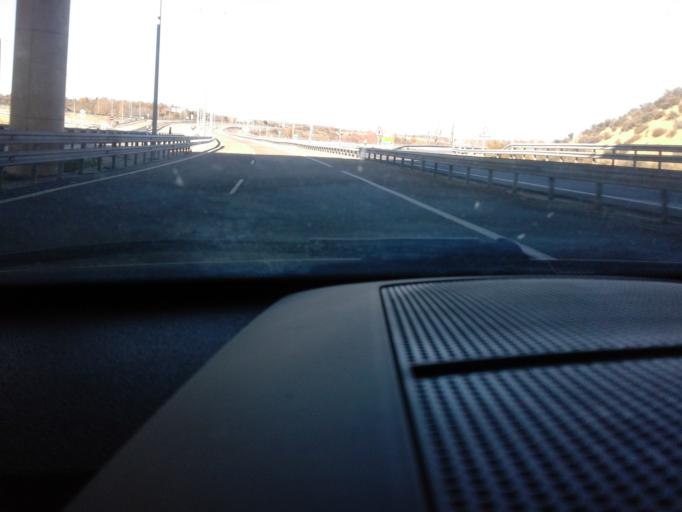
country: ES
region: Castille and Leon
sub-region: Provincia de Leon
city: Valverde de la Virgen
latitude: 42.5683
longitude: -5.6533
